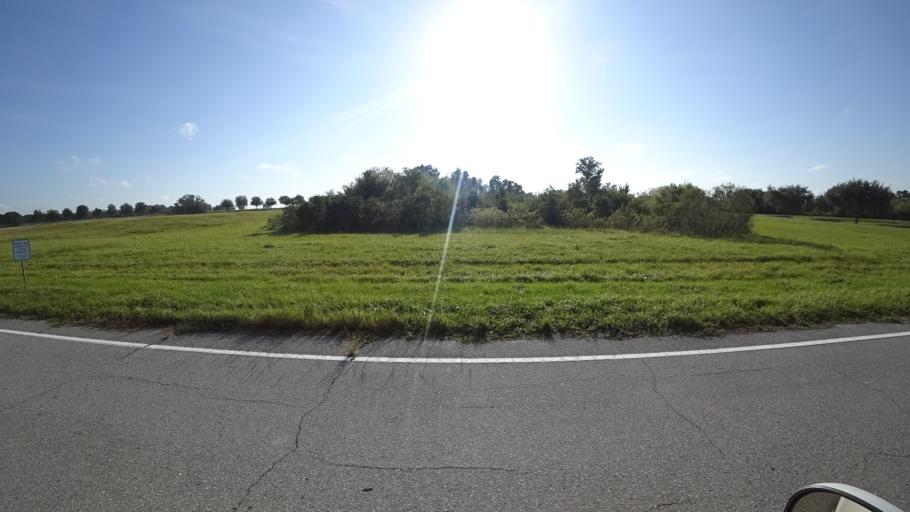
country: US
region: Florida
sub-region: Hillsborough County
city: Sun City Center
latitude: 27.5710
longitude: -82.3546
